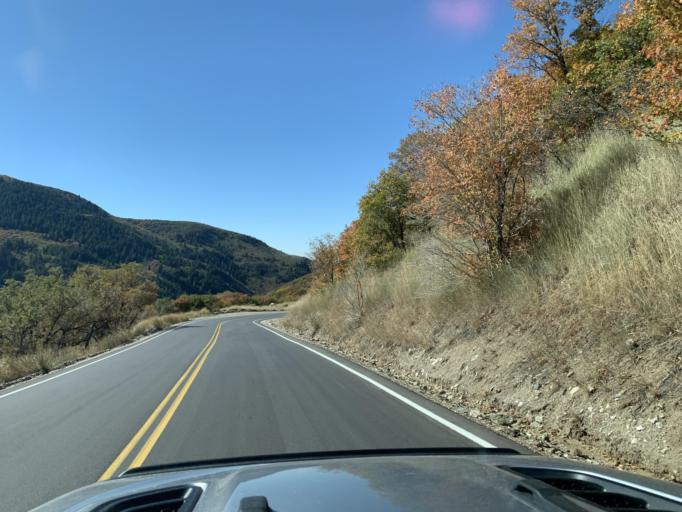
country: US
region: Utah
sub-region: Weber County
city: Liberty
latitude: 41.3186
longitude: -111.9057
